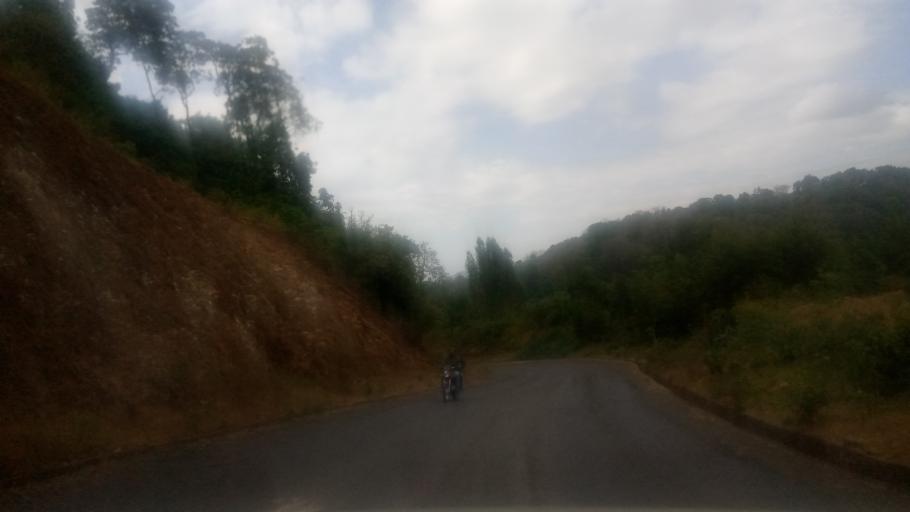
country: ET
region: Southern Nations, Nationalities, and People's Region
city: Bonga
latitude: 7.1114
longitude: 36.7430
